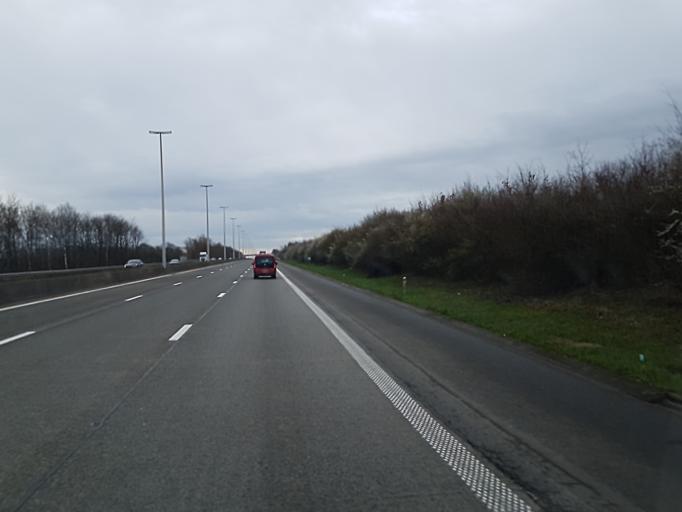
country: BE
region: Flanders
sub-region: Provincie Vlaams-Brabant
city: Tienen
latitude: 50.7636
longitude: 4.9411
